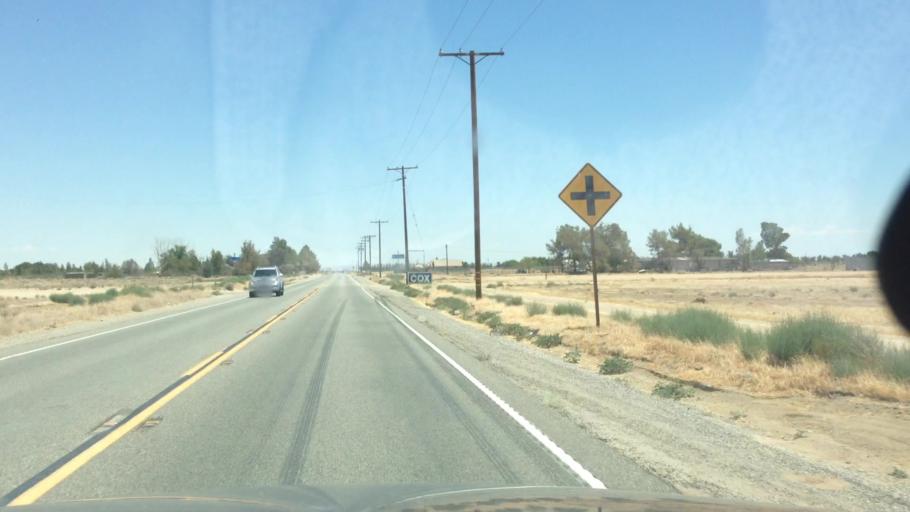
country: US
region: California
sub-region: Los Angeles County
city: Quartz Hill
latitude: 34.7764
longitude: -118.2825
